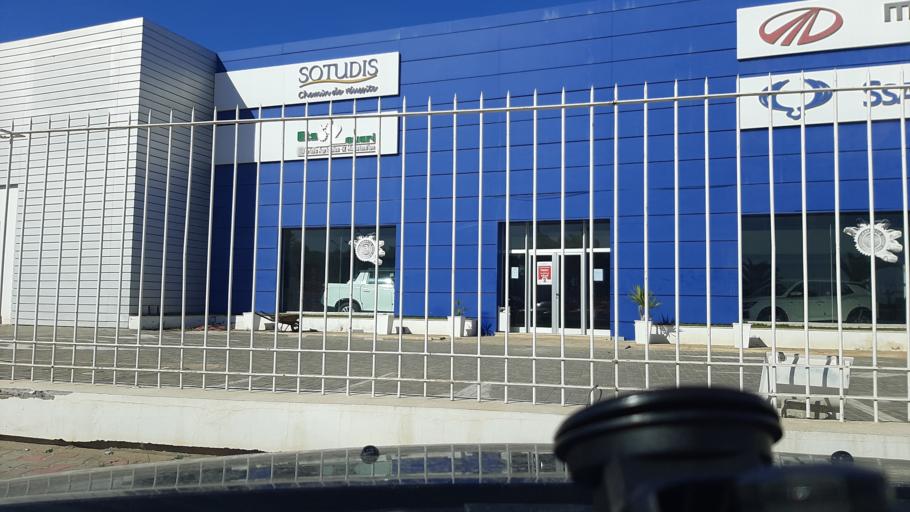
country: TN
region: Safaqis
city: Sfax
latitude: 34.7210
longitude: 10.7329
